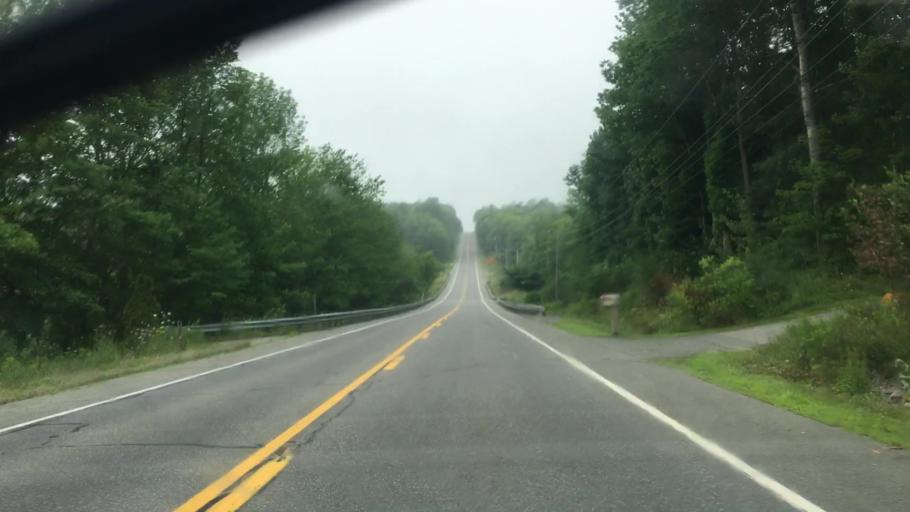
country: US
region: Maine
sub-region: Lincoln County
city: Wiscasset
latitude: 44.0737
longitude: -69.6965
